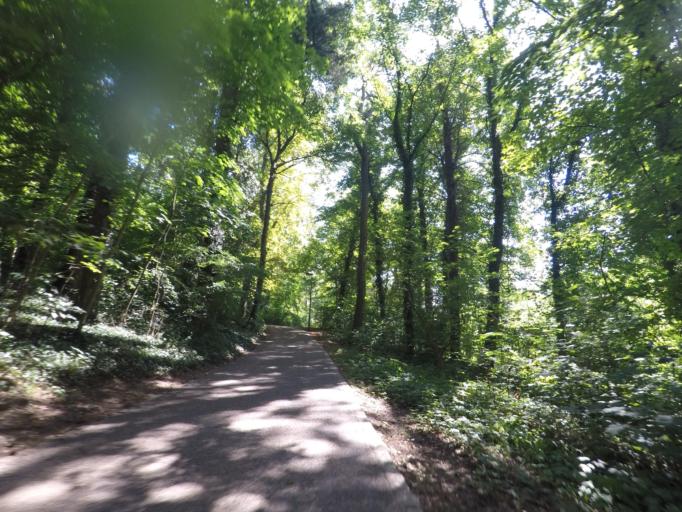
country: LU
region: Luxembourg
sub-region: Canton de Luxembourg
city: Luxembourg
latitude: 49.6244
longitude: 6.1315
